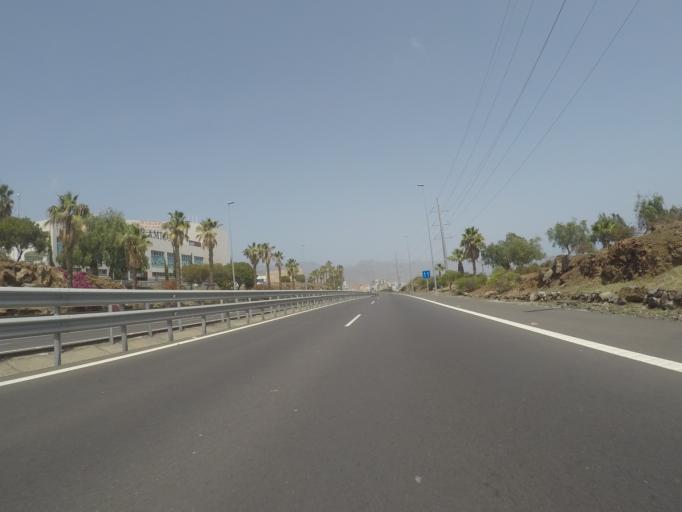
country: ES
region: Canary Islands
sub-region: Provincia de Santa Cruz de Tenerife
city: Santa Cruz de Tenerife
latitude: 28.4474
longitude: -16.2745
